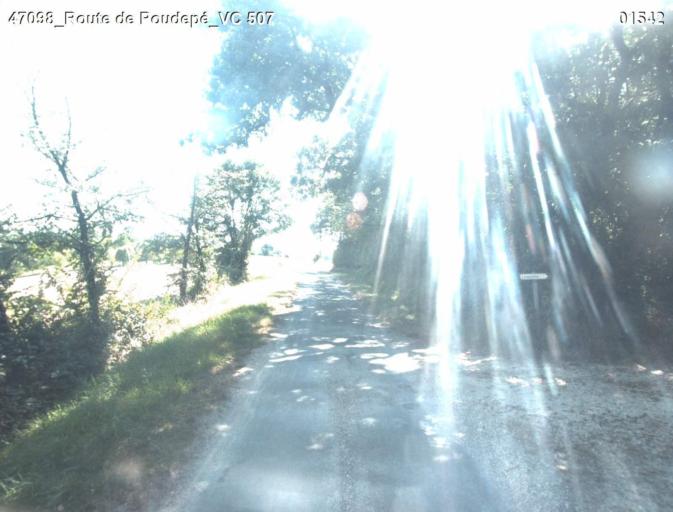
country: FR
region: Aquitaine
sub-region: Departement du Lot-et-Garonne
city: Nerac
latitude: 44.1061
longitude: 0.4031
